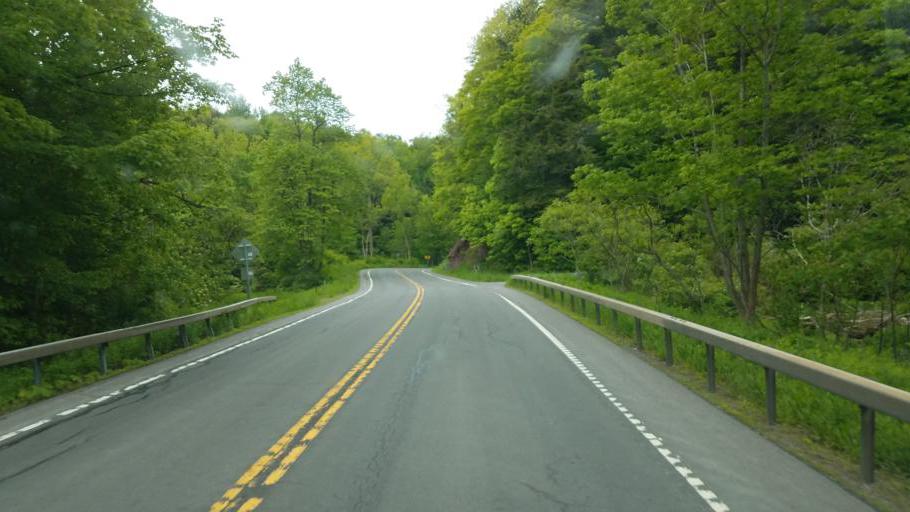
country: US
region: New York
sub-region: Herkimer County
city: Frankfort
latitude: 42.9625
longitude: -75.1031
